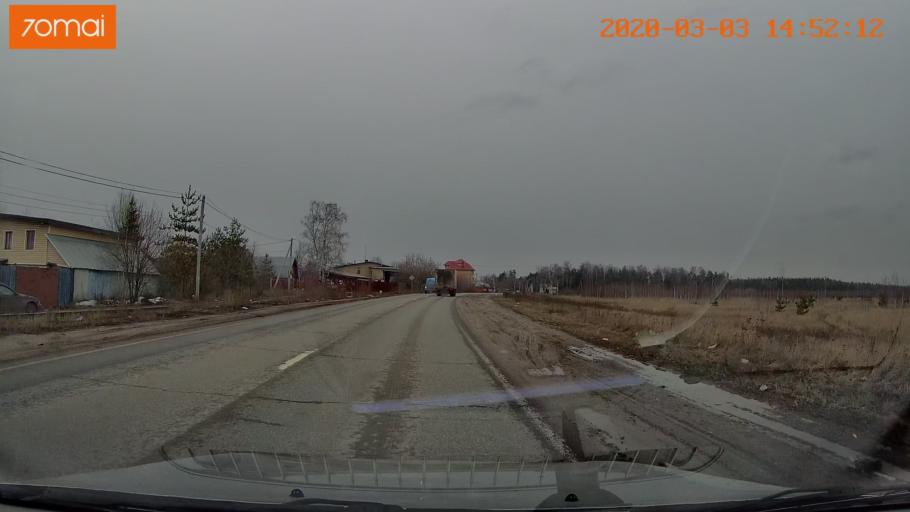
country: RU
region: Moskovskaya
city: Korenevo
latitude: 55.6688
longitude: 38.0175
